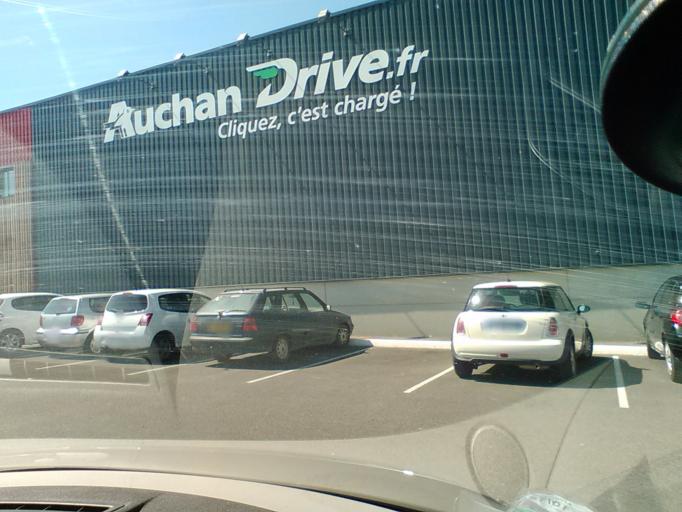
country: FR
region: Languedoc-Roussillon
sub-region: Departement de l'Herault
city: Perols
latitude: 43.5720
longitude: 3.9396
